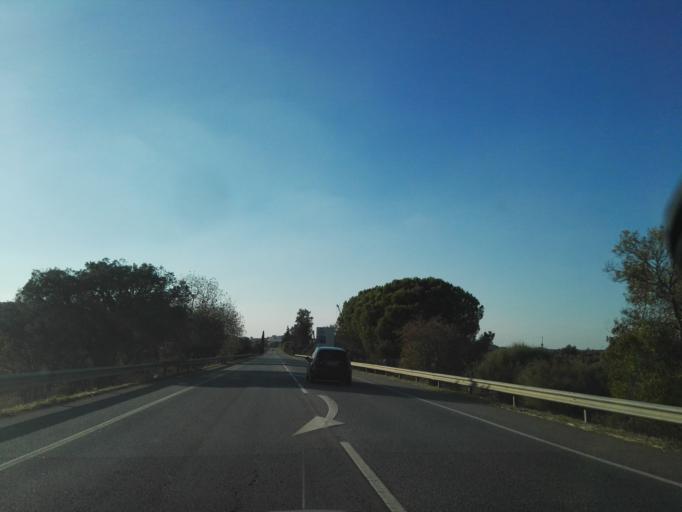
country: PT
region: Evora
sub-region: Estremoz
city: Estremoz
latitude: 38.8345
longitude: -7.5626
